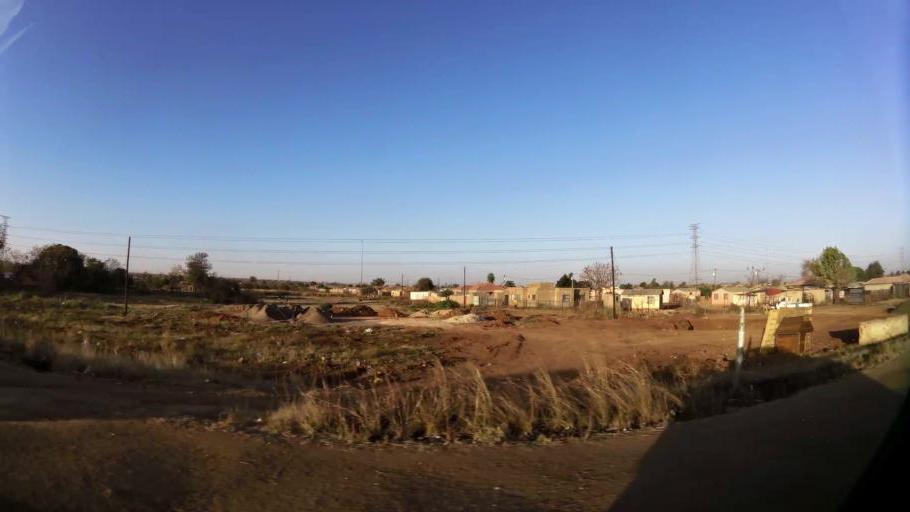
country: ZA
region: North-West
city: Ga-Rankuwa
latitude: -25.5894
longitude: 28.0754
